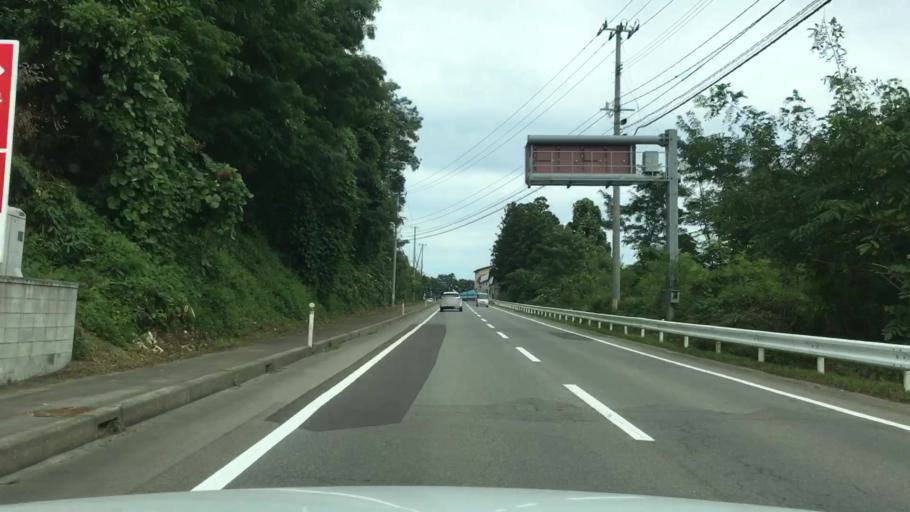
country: JP
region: Aomori
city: Shimokizukuri
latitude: 40.7639
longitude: 140.2247
